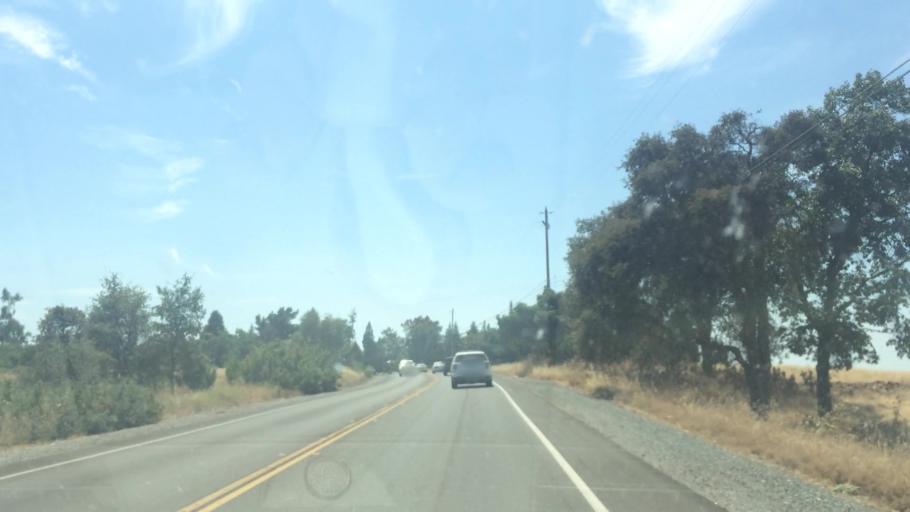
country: US
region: California
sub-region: Amador County
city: Sutter Creek
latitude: 38.3861
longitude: -120.7832
